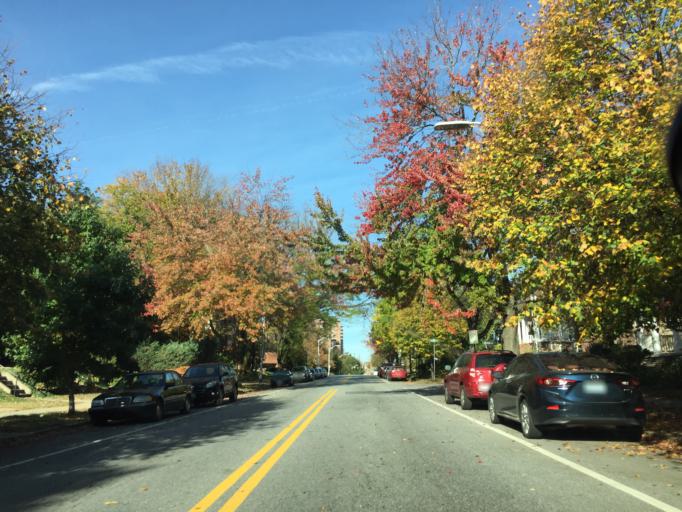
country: US
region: Maryland
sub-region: City of Baltimore
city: Baltimore
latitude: 39.3292
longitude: -76.6124
